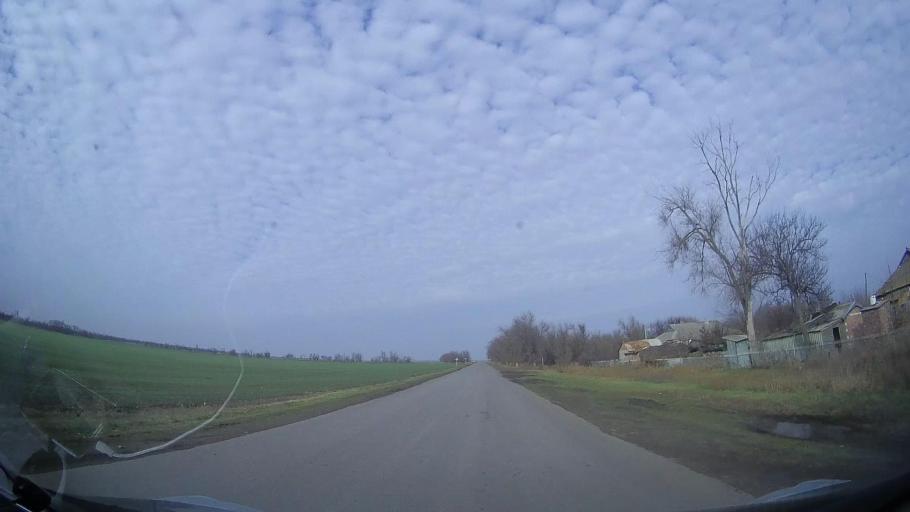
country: RU
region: Rostov
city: Gigant
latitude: 46.9246
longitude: 41.2472
